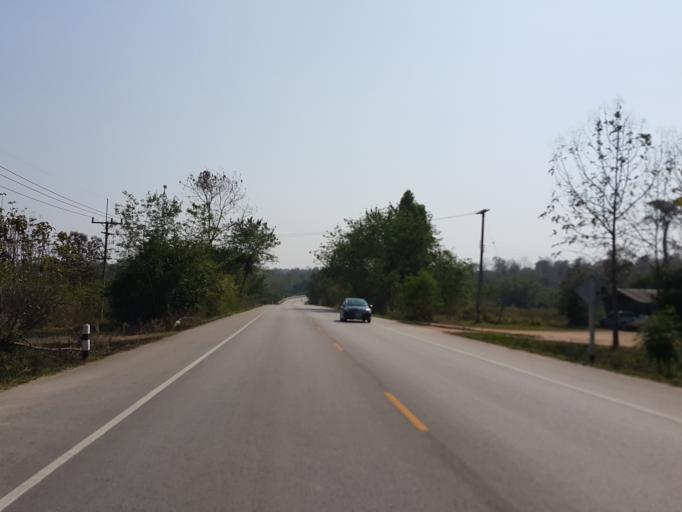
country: TH
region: Lampang
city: Wang Nuea
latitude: 18.9663
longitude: 99.6122
